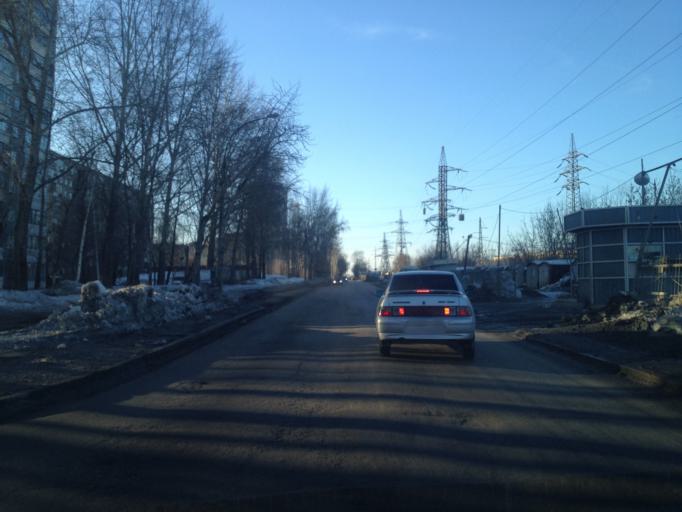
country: RU
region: Sverdlovsk
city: Yekaterinburg
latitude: 56.8706
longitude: 60.5622
